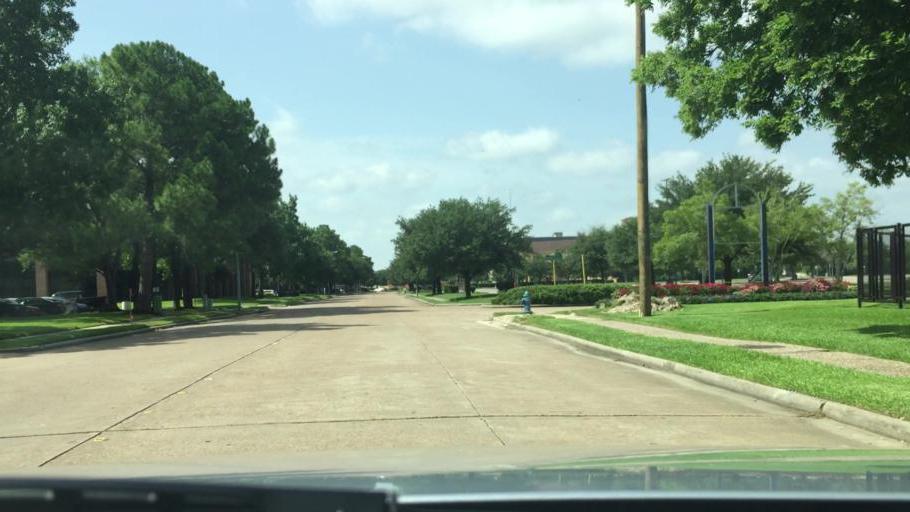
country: US
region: Texas
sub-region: Harris County
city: Hudson
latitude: 29.8477
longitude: -95.4949
